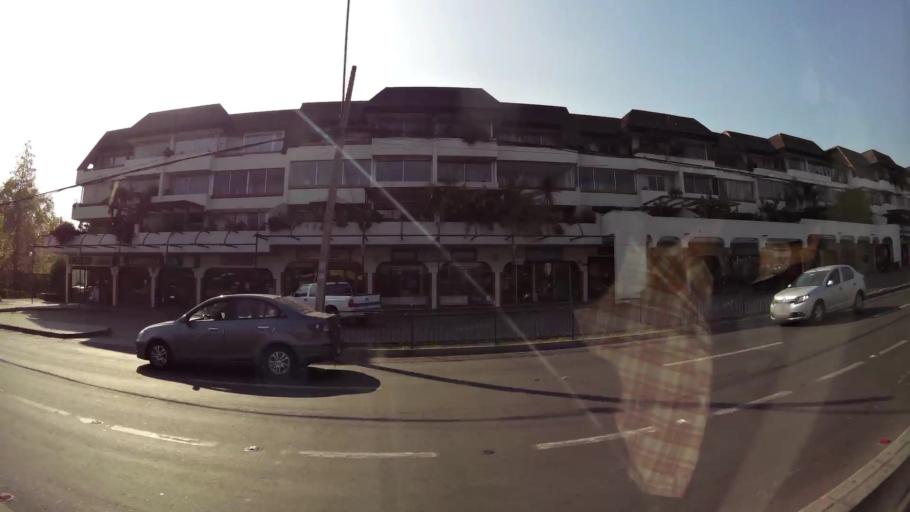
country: CL
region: Santiago Metropolitan
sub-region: Provincia de Santiago
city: Villa Presidente Frei, Nunoa, Santiago, Chile
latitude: -33.3835
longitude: -70.5506
